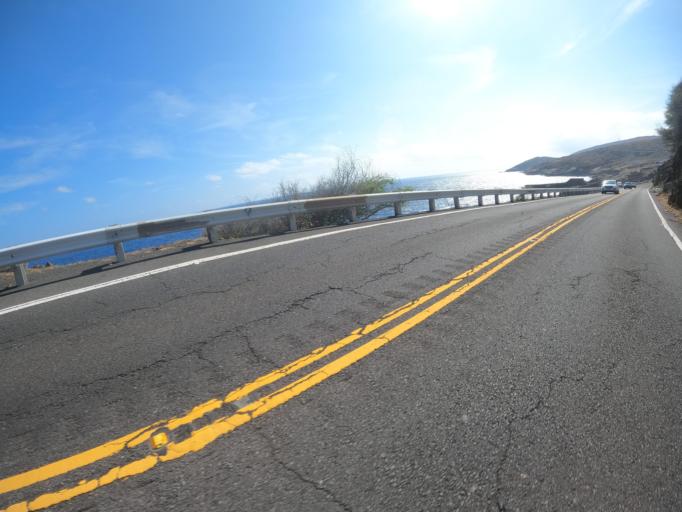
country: US
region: Hawaii
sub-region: Honolulu County
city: Waimanalo Beach
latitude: 21.2784
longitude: -157.6820
